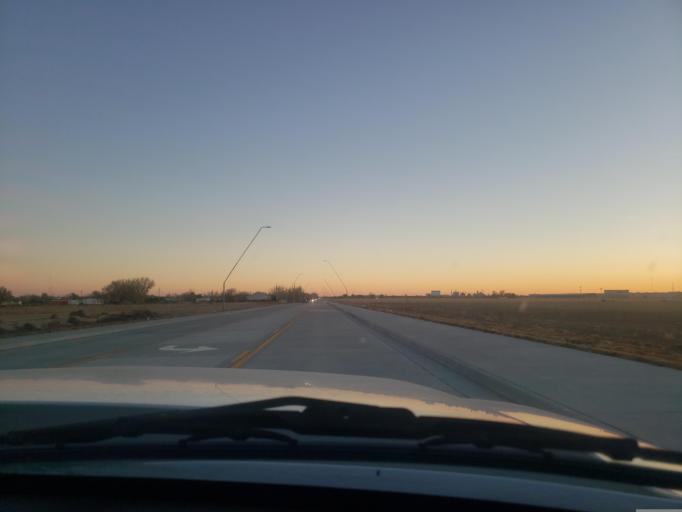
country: US
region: Kansas
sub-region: Finney County
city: Garden City
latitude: 37.9845
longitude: -100.8290
